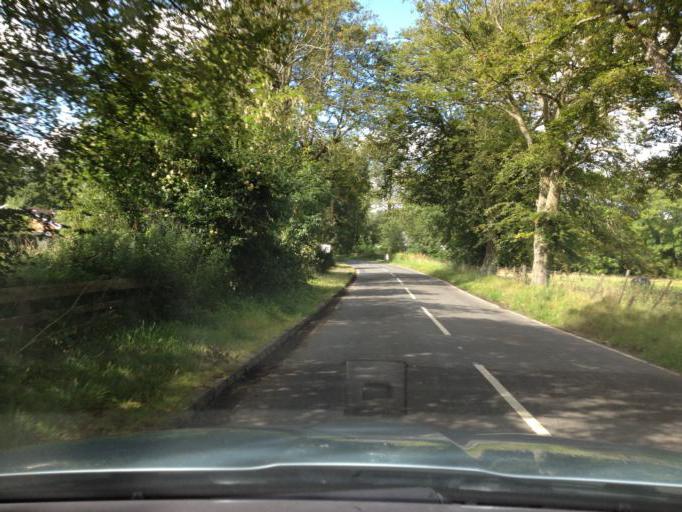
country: GB
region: Scotland
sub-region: West Lothian
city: Armadale
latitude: 55.9227
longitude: -3.6922
